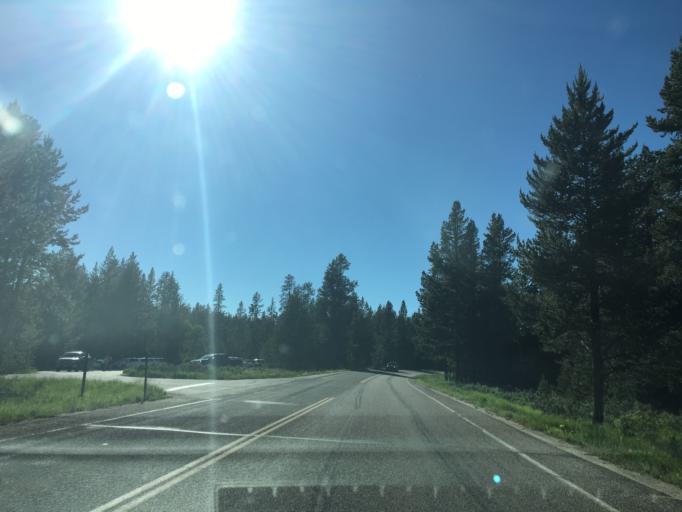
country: US
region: Wyoming
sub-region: Teton County
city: Jackson
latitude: 43.8453
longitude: -110.5147
